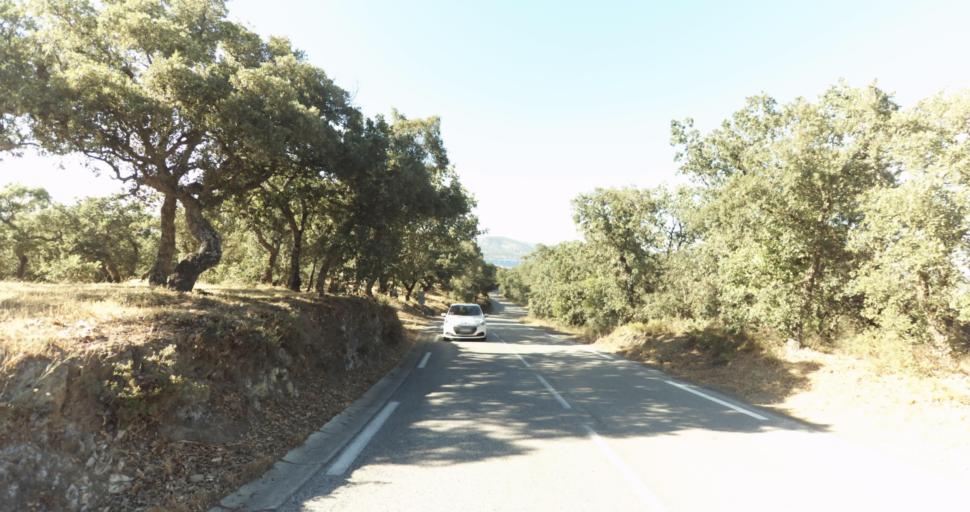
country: FR
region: Provence-Alpes-Cote d'Azur
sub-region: Departement du Var
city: Gassin
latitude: 43.2326
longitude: 6.5856
